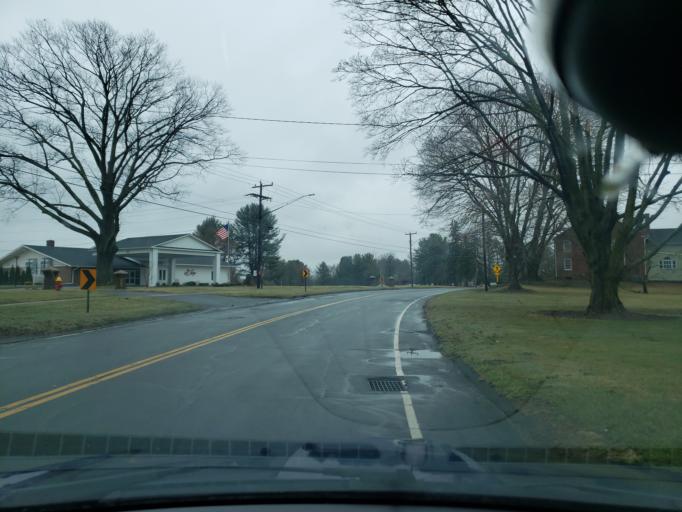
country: US
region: Connecticut
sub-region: Hartford County
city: South Windsor
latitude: 41.8208
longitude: -72.6527
